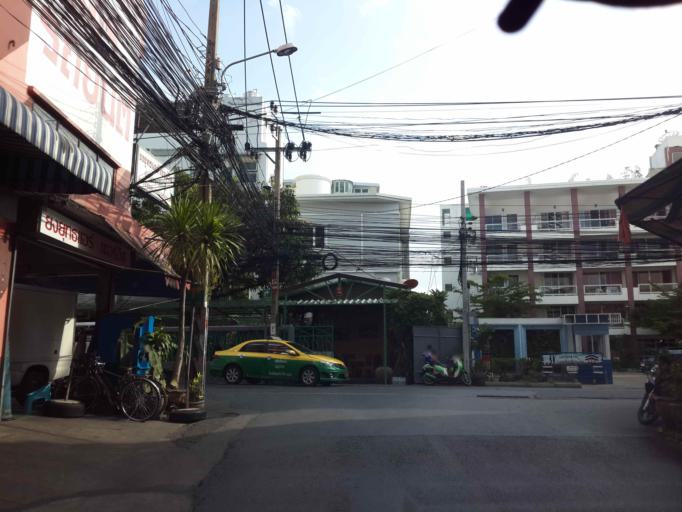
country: TH
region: Bangkok
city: Khlong Toei
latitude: 13.7198
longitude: 100.5487
